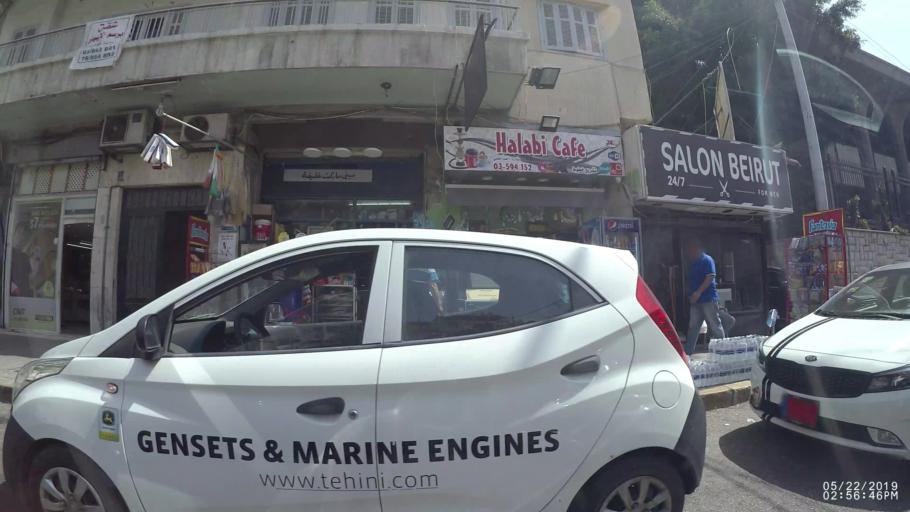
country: LB
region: Beyrouth
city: Ra's Bayrut
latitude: 33.8938
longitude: 35.4838
